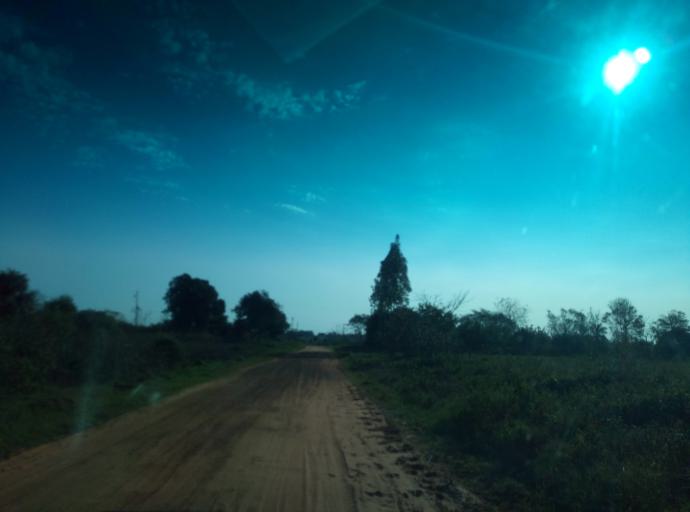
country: PY
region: Caaguazu
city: Doctor Cecilio Baez
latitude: -25.1647
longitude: -56.2307
